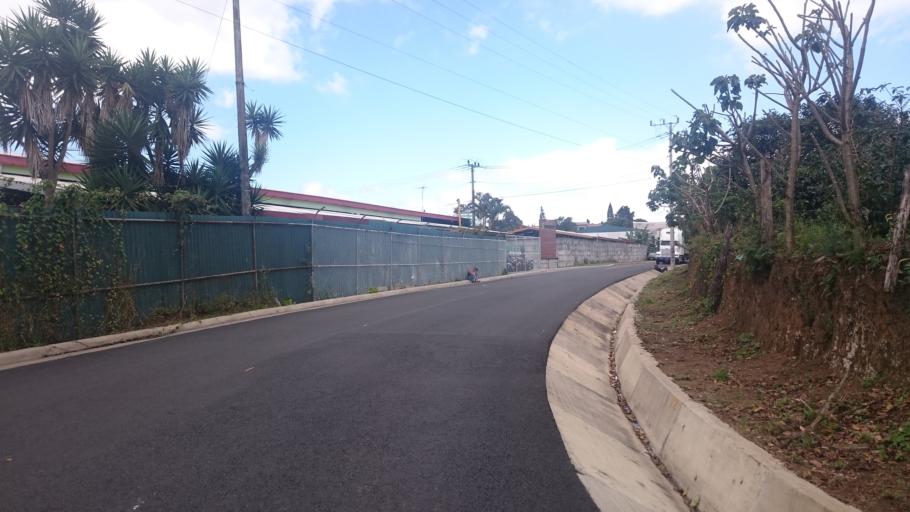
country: CR
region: San Jose
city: Curridabat
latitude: 9.9201
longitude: -84.0285
